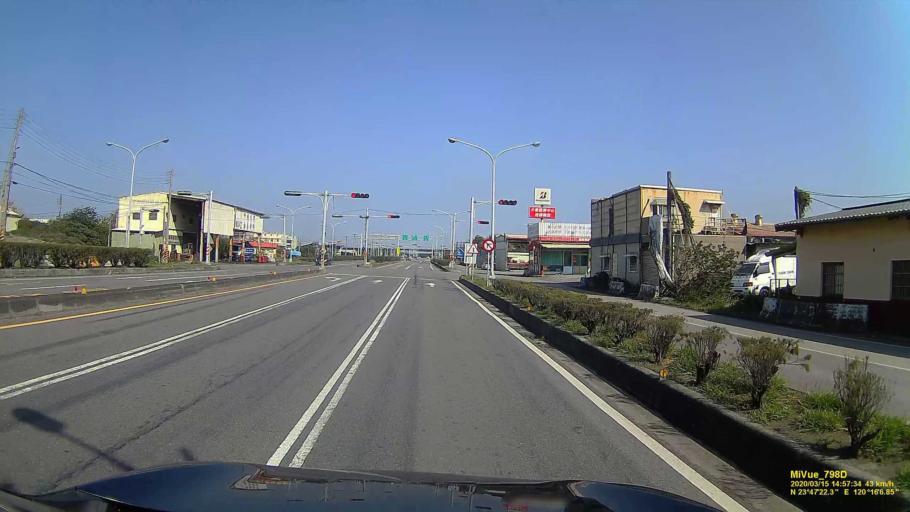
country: TW
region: Taiwan
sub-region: Yunlin
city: Douliu
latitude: 23.7895
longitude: 120.2687
